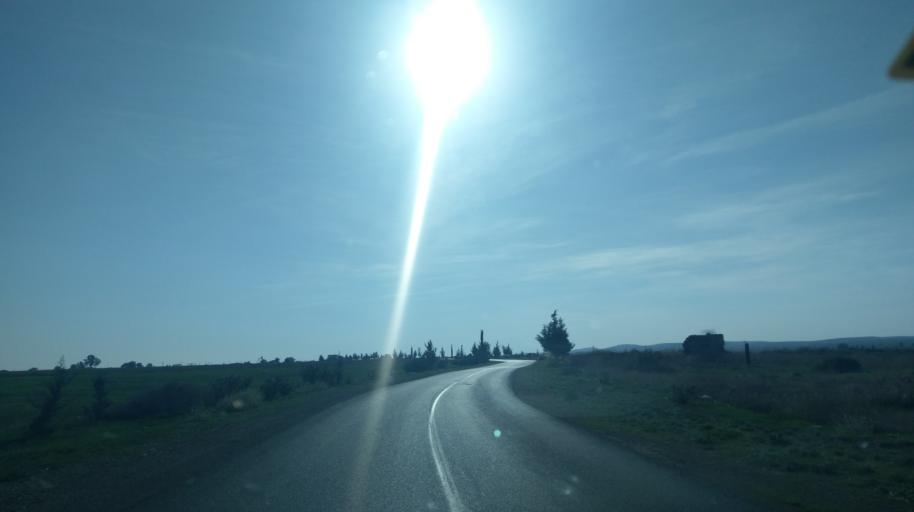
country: CY
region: Larnaka
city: Pergamos
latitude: 35.0749
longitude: 33.7196
